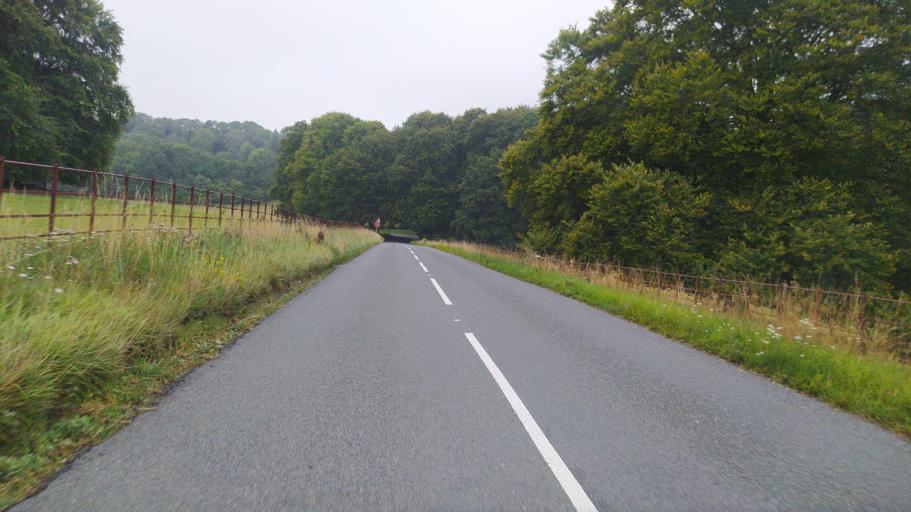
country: GB
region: England
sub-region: Wiltshire
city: Ansty
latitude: 50.9508
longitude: -2.0611
